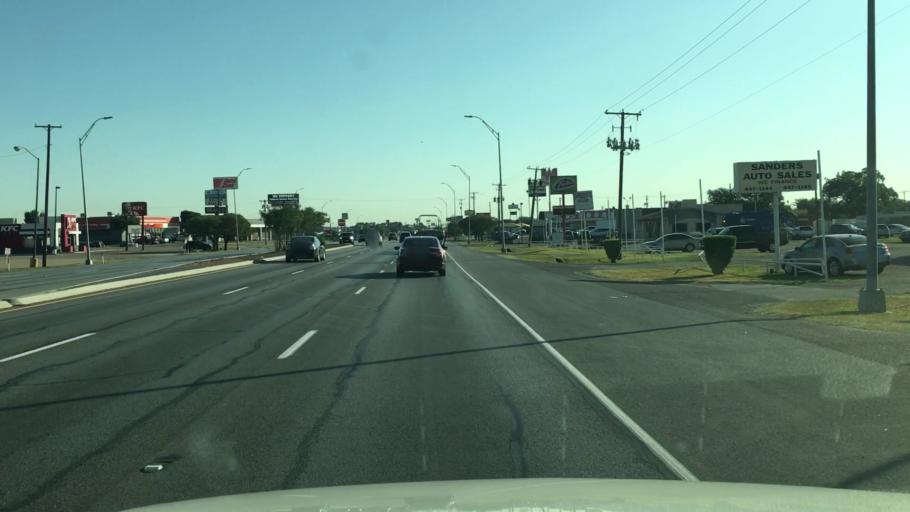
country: US
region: Texas
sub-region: Johnson County
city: Burleson
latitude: 32.5350
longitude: -97.3354
